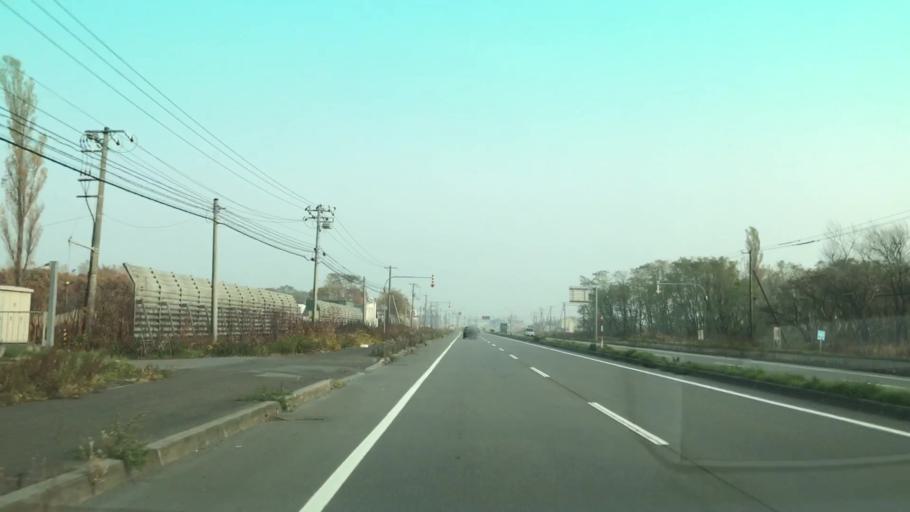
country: JP
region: Hokkaido
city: Ishikari
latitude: 43.2101
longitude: 141.3338
